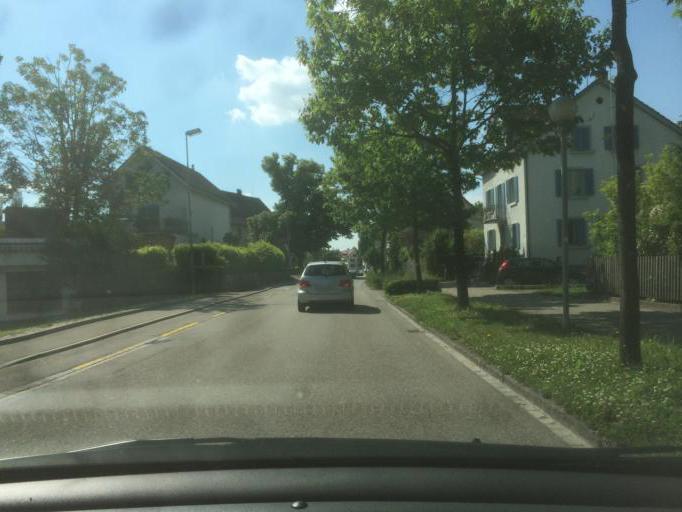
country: CH
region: Zurich
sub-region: Bezirk Hinwil
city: Wetzikon
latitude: 47.3278
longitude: 8.7924
